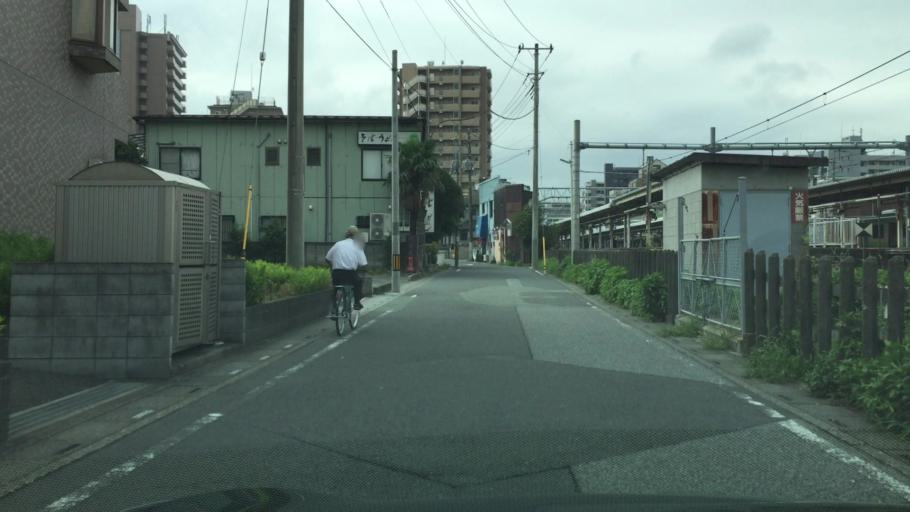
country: JP
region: Saitama
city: Ageoshimo
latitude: 35.9426
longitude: 139.6092
